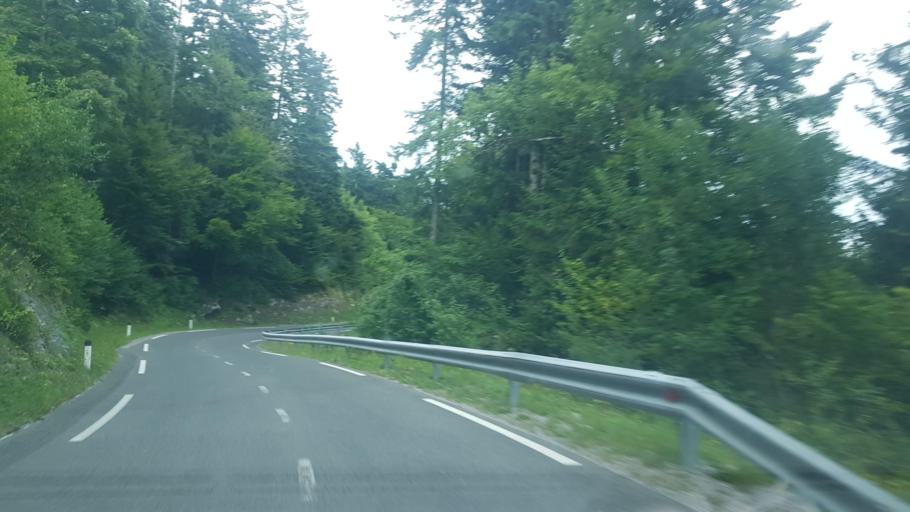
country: SI
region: Logatec
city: Logatec
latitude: 45.8676
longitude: 14.1239
